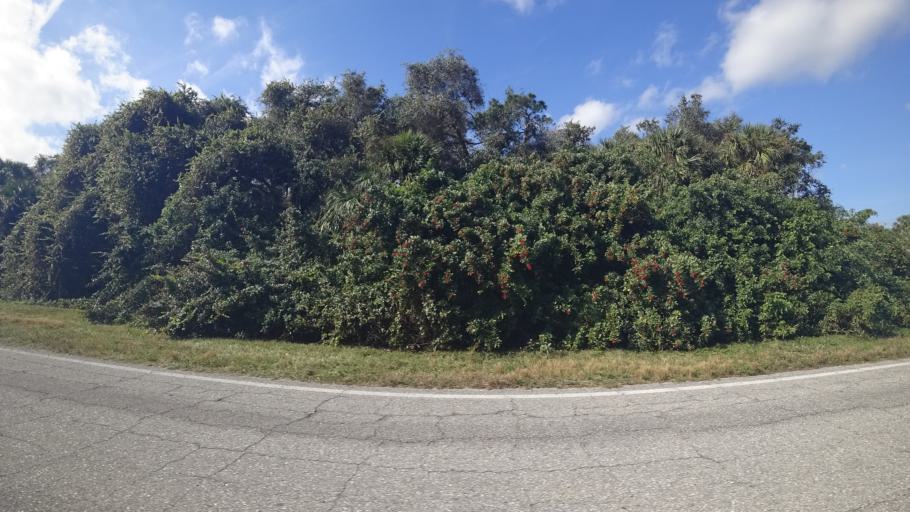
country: US
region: Florida
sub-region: Charlotte County
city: Port Charlotte
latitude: 27.0605
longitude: -82.1164
